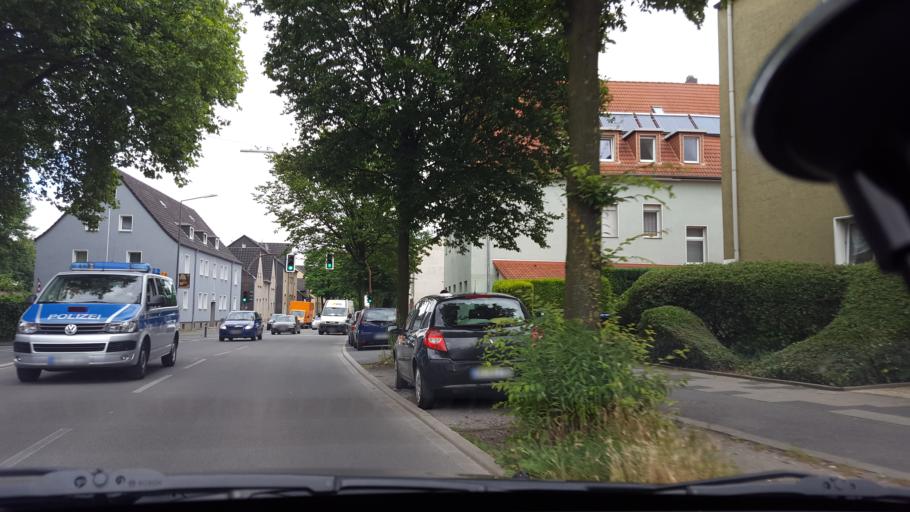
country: DE
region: North Rhine-Westphalia
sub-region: Regierungsbezirk Munster
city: Recklinghausen
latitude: 51.6201
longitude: 7.2242
